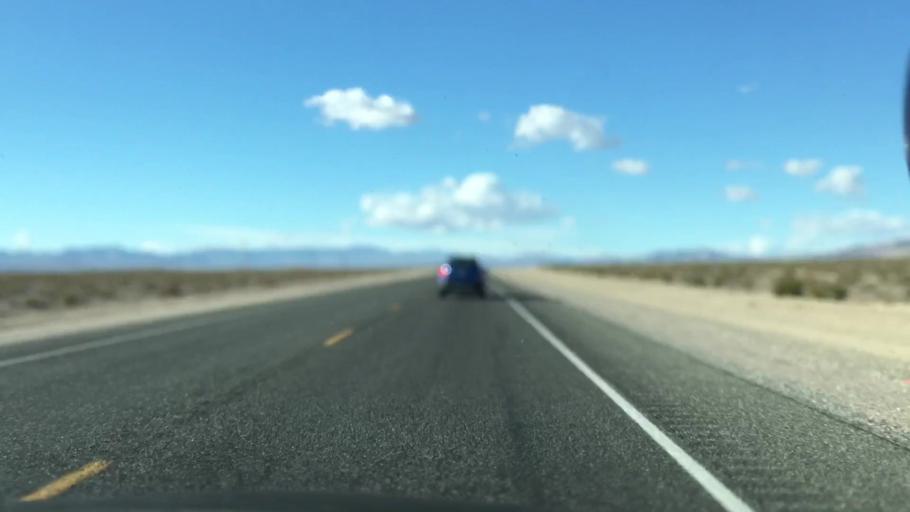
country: US
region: Nevada
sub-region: Nye County
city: Beatty
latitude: 36.7261
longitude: -116.6254
